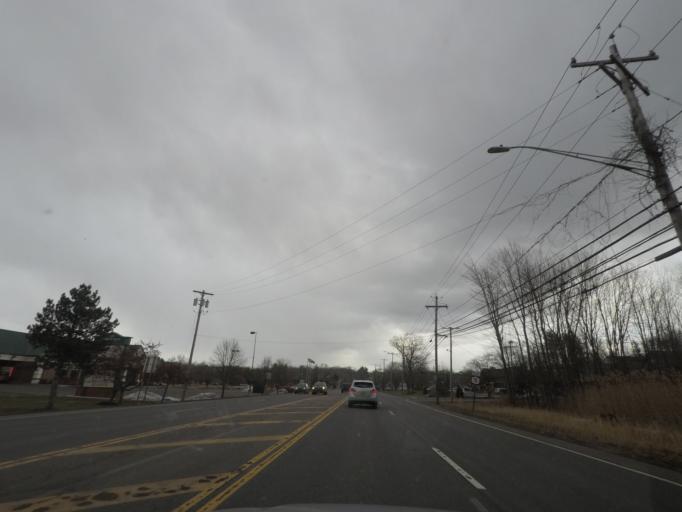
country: US
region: New York
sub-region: Onondaga County
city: Fayetteville
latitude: 43.0291
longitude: -76.0198
